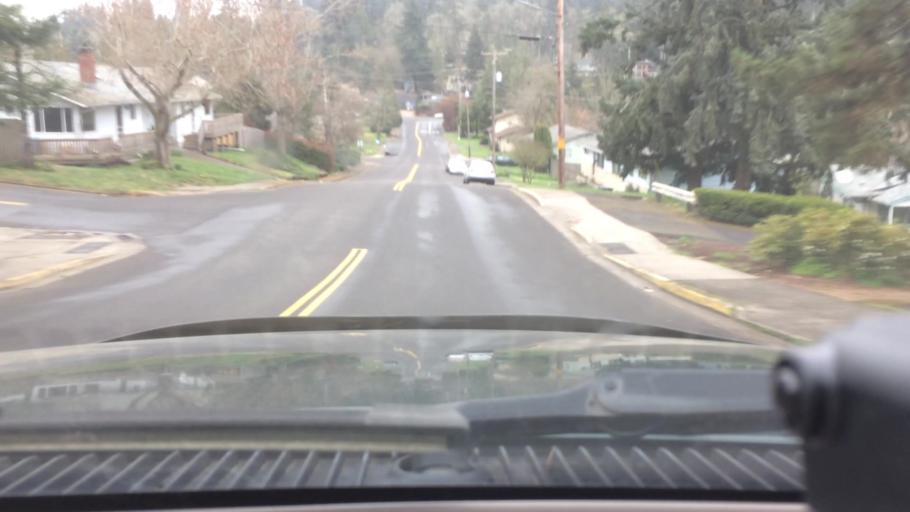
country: US
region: Oregon
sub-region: Lane County
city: Eugene
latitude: 44.0293
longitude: -123.1013
